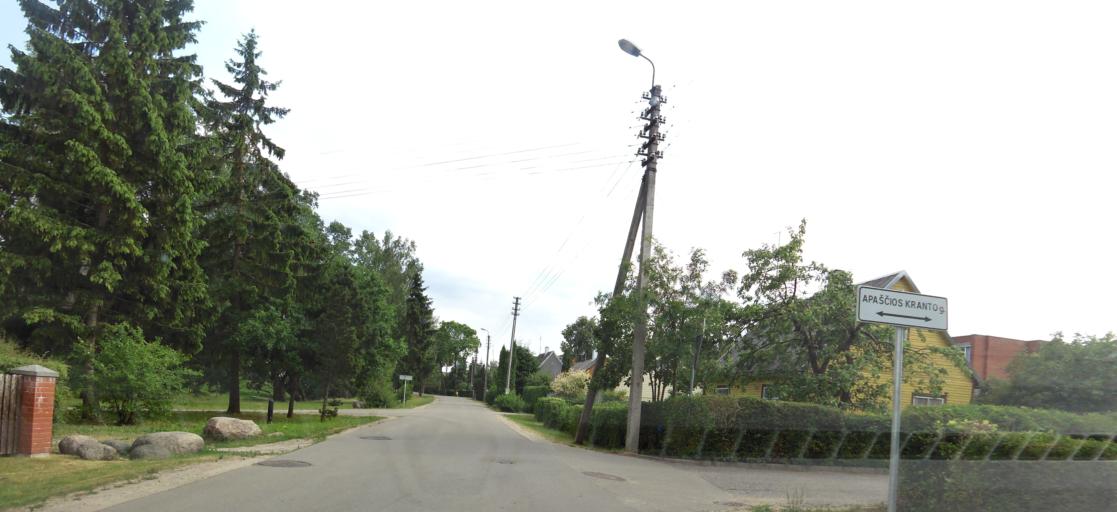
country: LT
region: Panevezys
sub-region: Birzai
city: Birzai
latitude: 56.1988
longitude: 24.7604
